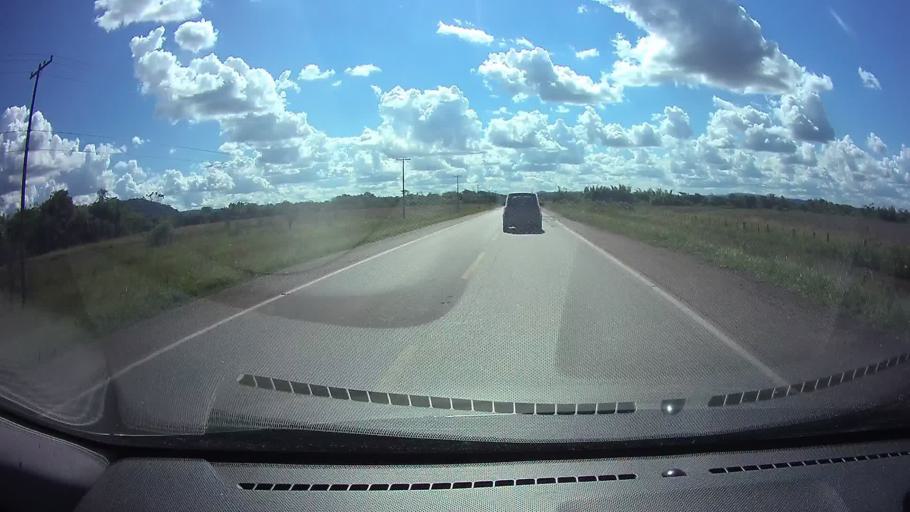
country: PY
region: Paraguari
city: La Colmena
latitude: -25.7534
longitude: -56.7766
